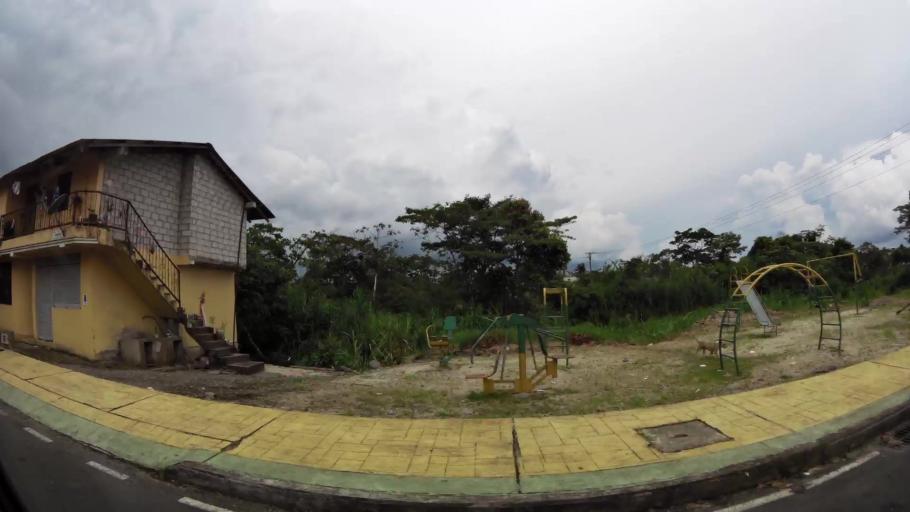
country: EC
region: Pastaza
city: Puyo
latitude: -1.4931
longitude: -78.0095
